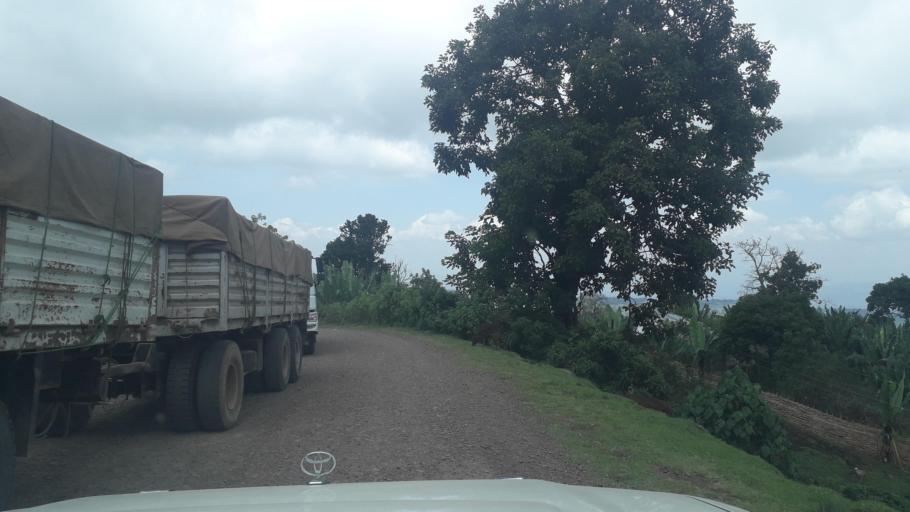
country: ET
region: Oromiya
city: Jima
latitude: 7.4500
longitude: 36.8739
